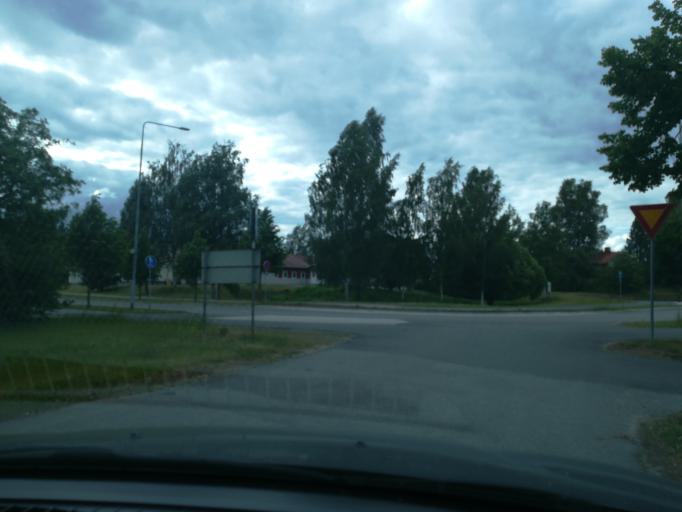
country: FI
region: Southern Savonia
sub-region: Mikkeli
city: Mikkeli
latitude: 61.6770
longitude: 27.2573
